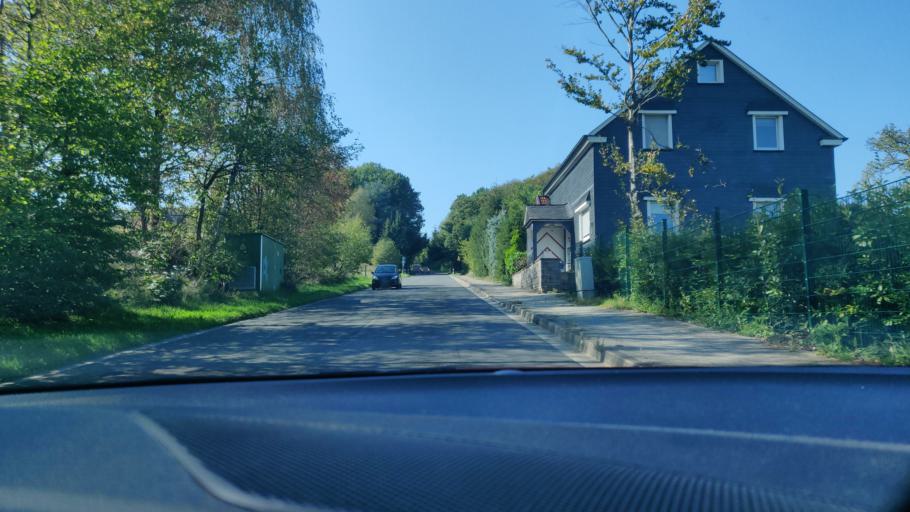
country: DE
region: North Rhine-Westphalia
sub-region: Regierungsbezirk Dusseldorf
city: Velbert
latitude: 51.3513
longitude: 7.0982
